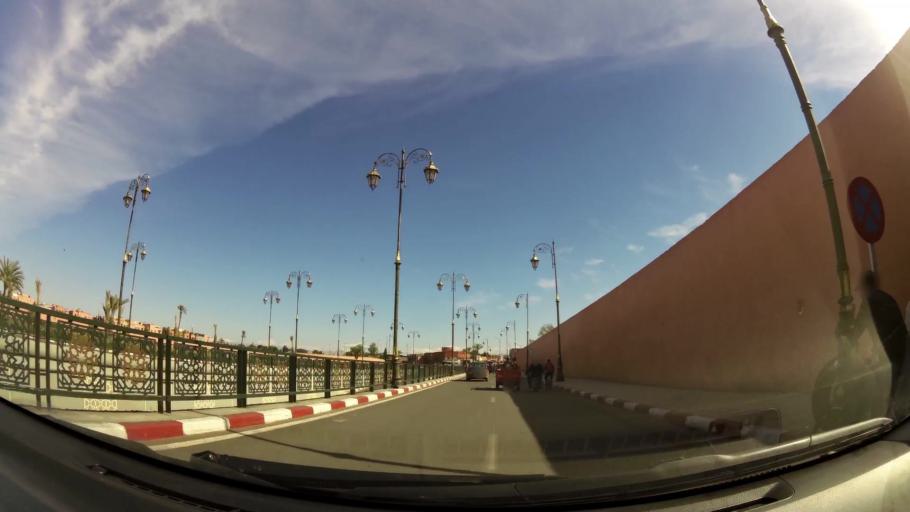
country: MA
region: Marrakech-Tensift-Al Haouz
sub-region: Marrakech
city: Marrakesh
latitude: 31.6439
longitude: -7.9872
